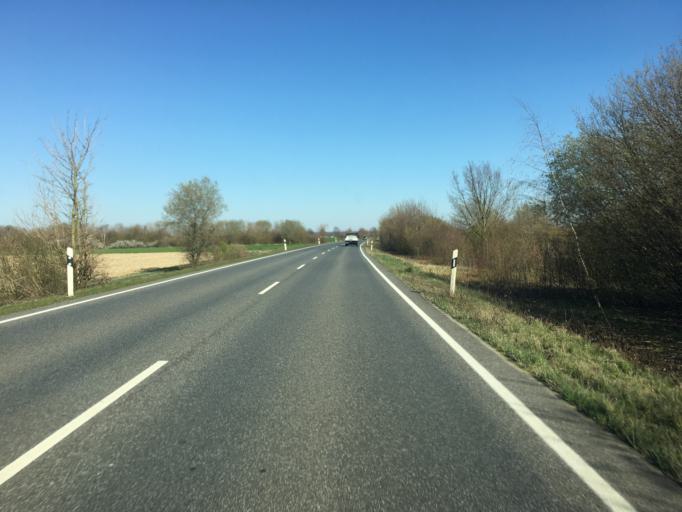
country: DE
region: North Rhine-Westphalia
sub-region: Regierungsbezirk Koln
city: Kerpen
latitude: 50.8511
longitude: 6.6630
